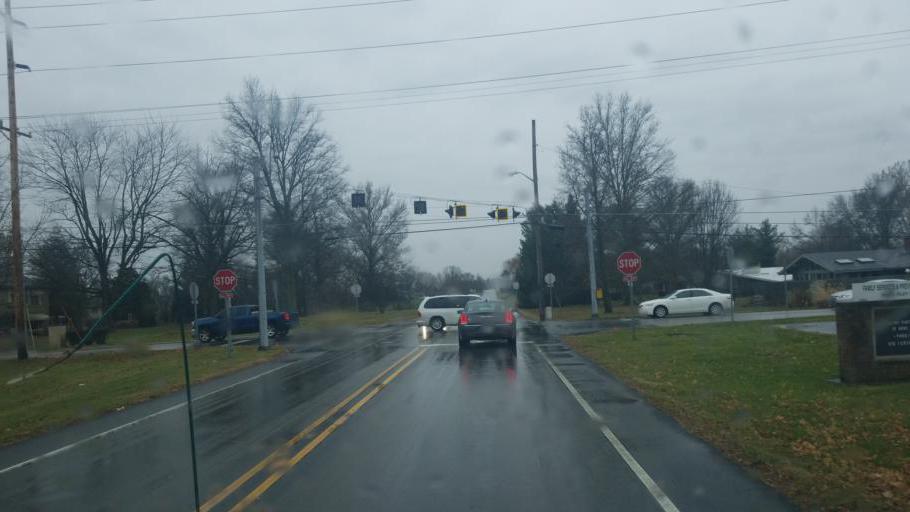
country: US
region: Indiana
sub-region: Shelby County
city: Shelbyville
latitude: 39.5050
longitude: -85.7709
